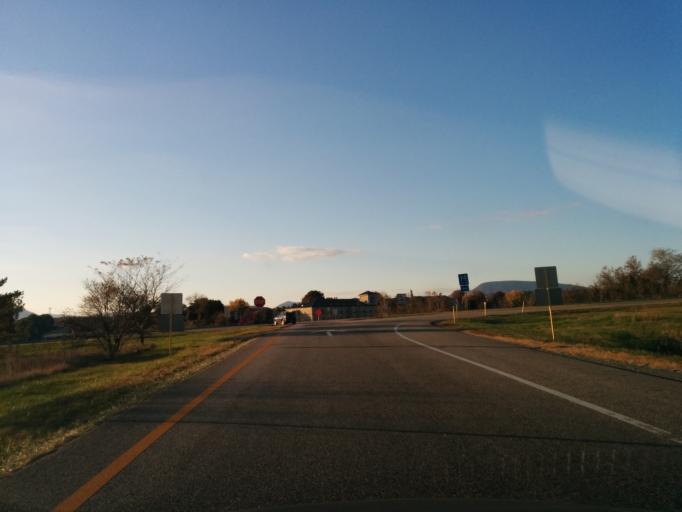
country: US
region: Virginia
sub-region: Rockbridge County
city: East Lexington
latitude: 37.8010
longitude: -79.4127
